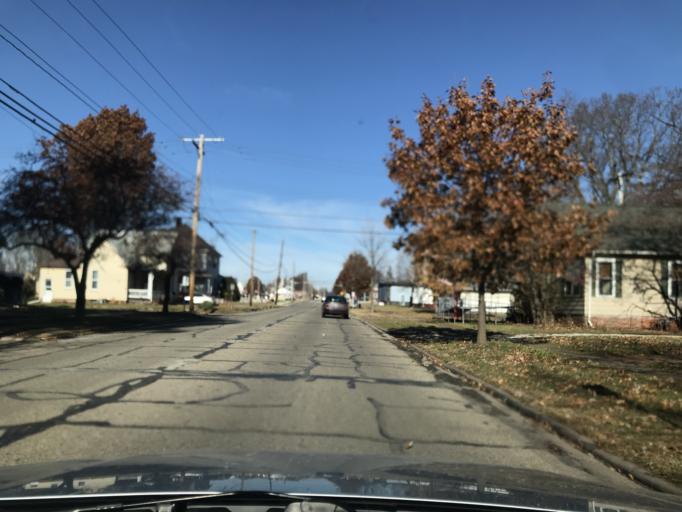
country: US
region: Illinois
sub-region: McDonough County
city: Macomb
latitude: 40.4566
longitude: -90.6672
